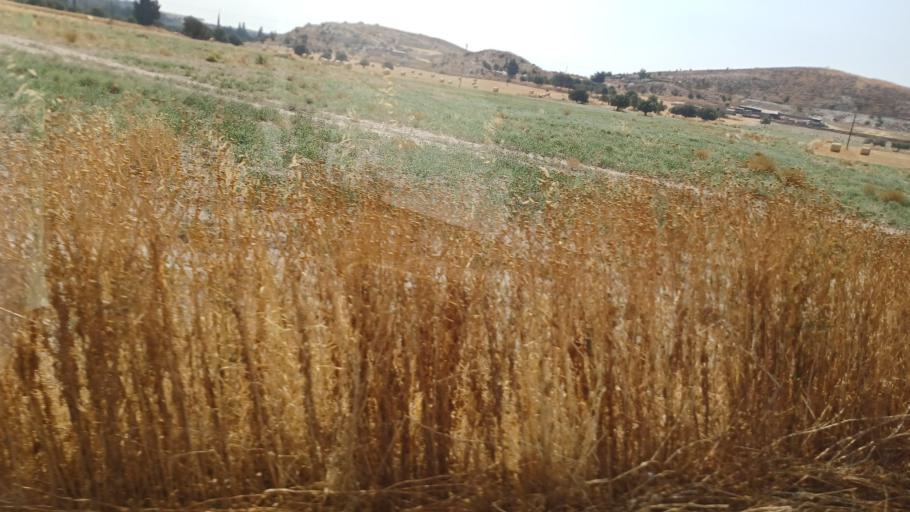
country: CY
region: Larnaka
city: Aradippou
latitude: 34.9216
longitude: 33.5378
